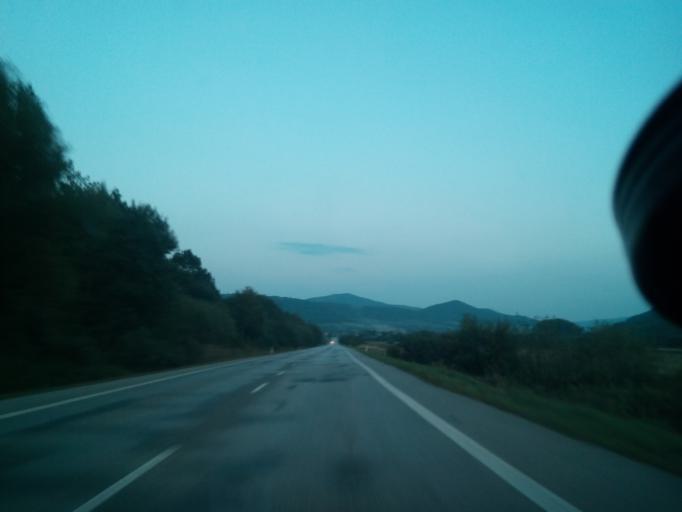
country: SK
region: Kosicky
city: Roznava
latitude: 48.7075
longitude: 20.4897
